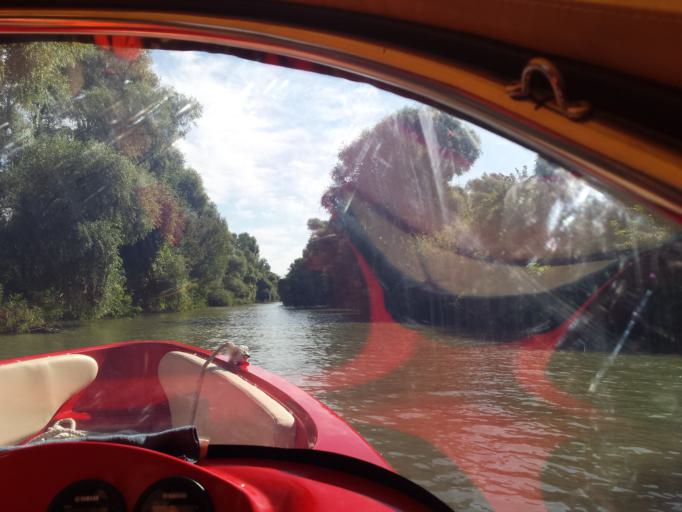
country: RO
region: Tulcea
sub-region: Comuna Pardina
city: Pardina
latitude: 45.2535
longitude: 28.9293
